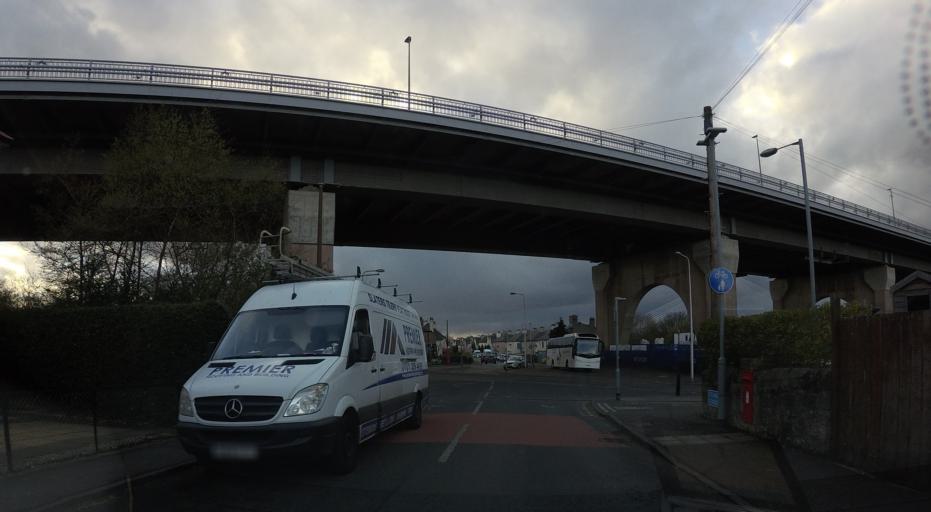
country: GB
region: Scotland
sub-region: Edinburgh
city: Queensferry
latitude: 55.9899
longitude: -3.4042
